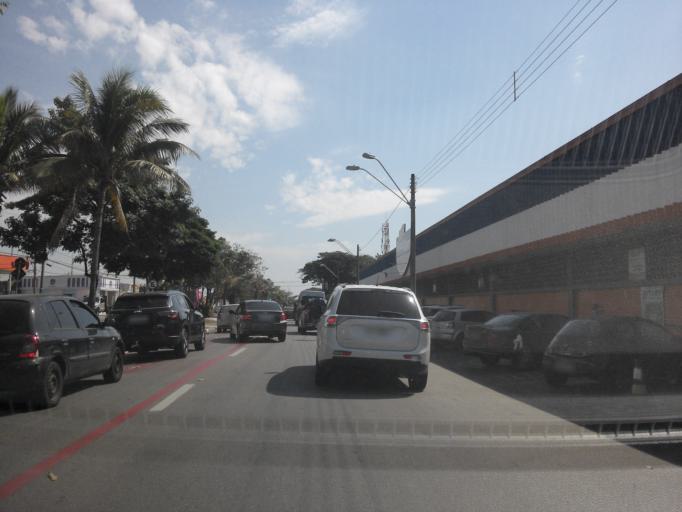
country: BR
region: Sao Paulo
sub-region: Sumare
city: Sumare
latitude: -22.8230
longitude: -47.2714
